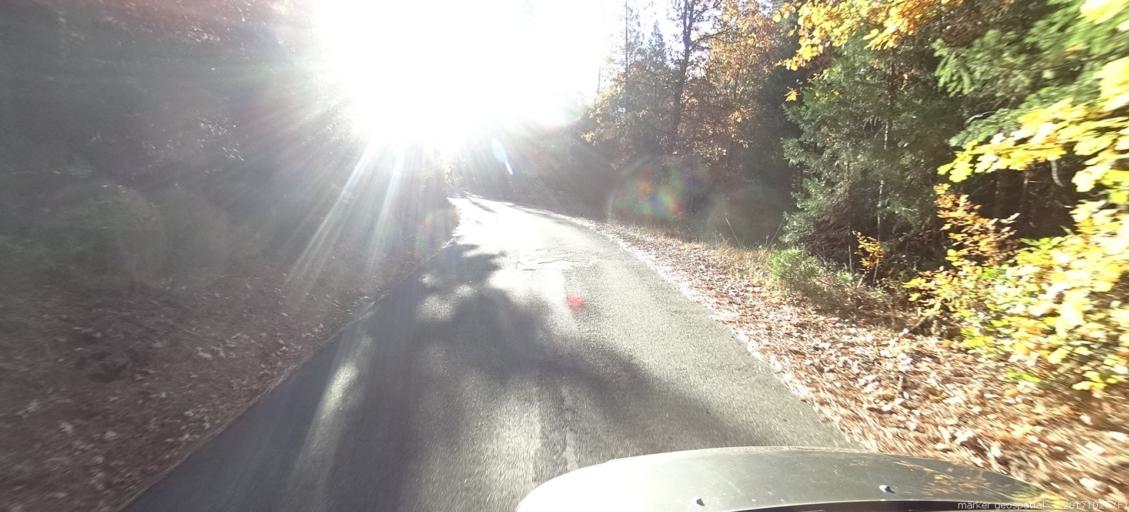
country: US
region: California
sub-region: Shasta County
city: Burney
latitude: 41.0120
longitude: -121.9021
